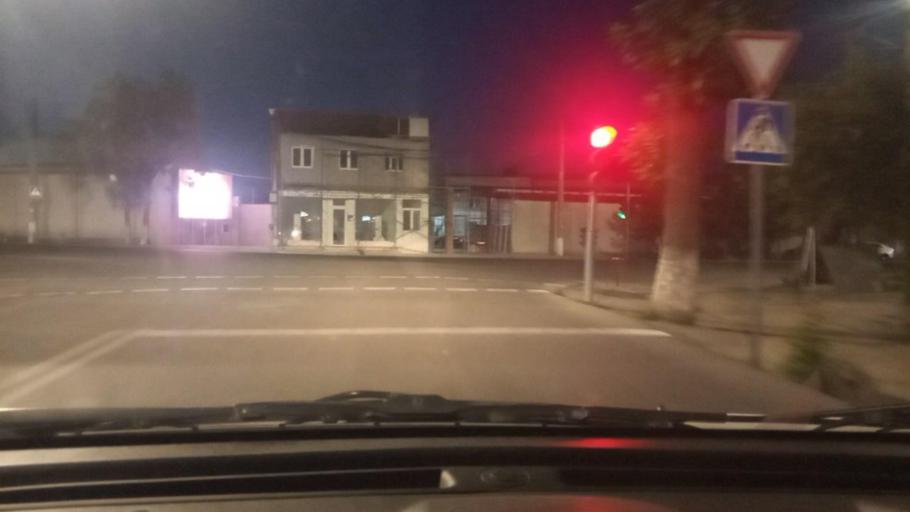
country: UZ
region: Toshkent Shahri
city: Tashkent
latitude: 41.2722
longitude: 69.2792
